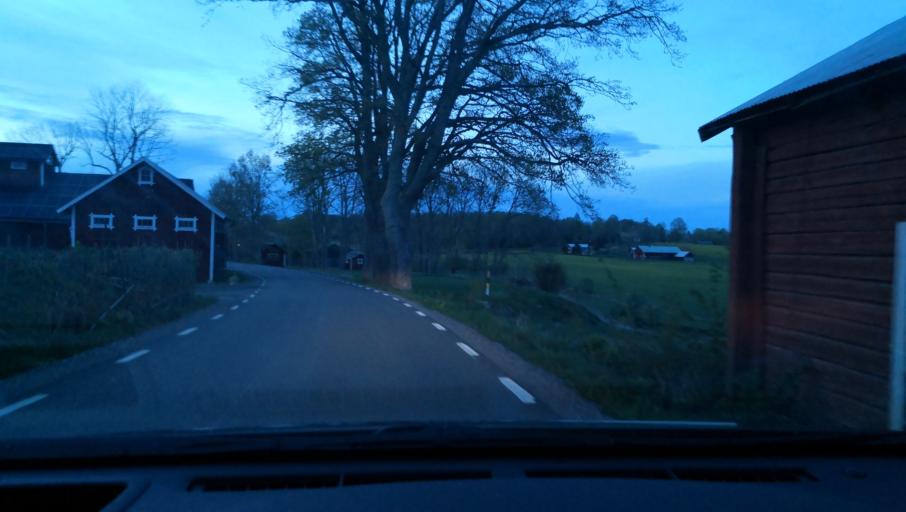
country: SE
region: OErebro
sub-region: Askersunds Kommun
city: Asbro
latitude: 59.0515
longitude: 14.9308
